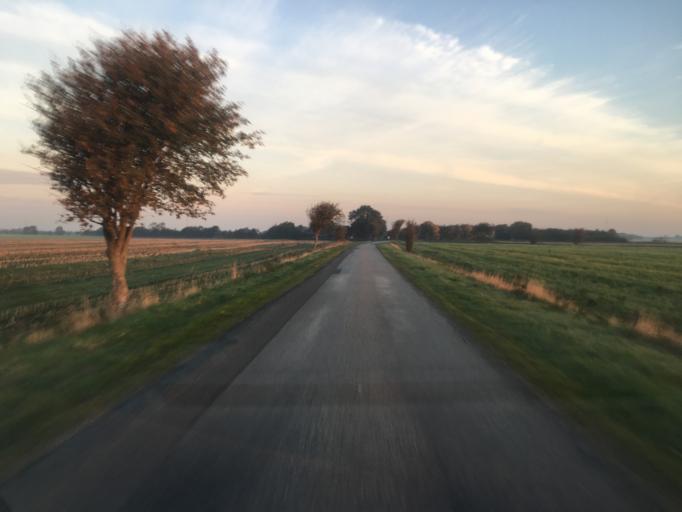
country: DK
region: South Denmark
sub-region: Tonder Kommune
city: Logumkloster
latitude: 55.0470
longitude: 9.0253
